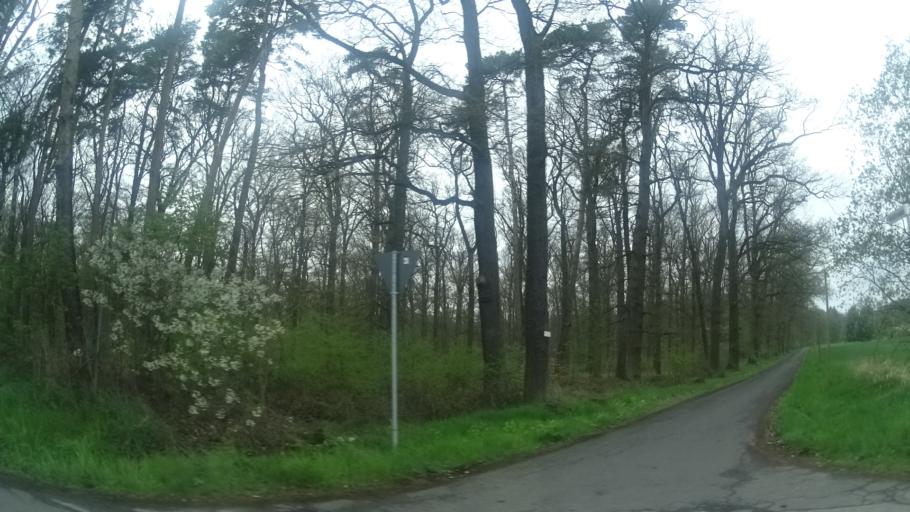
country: DE
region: Hesse
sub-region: Regierungsbezirk Giessen
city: Alten Buseck
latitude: 50.6134
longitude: 8.7288
